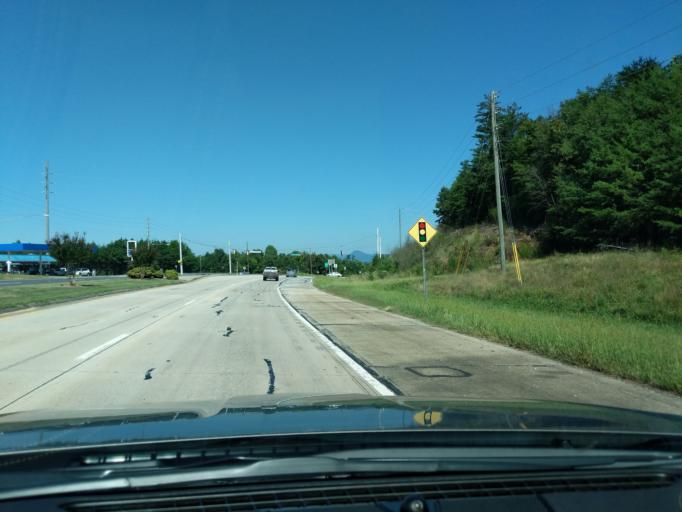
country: US
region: Georgia
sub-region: Habersham County
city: Baldwin
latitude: 34.4997
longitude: -83.5423
